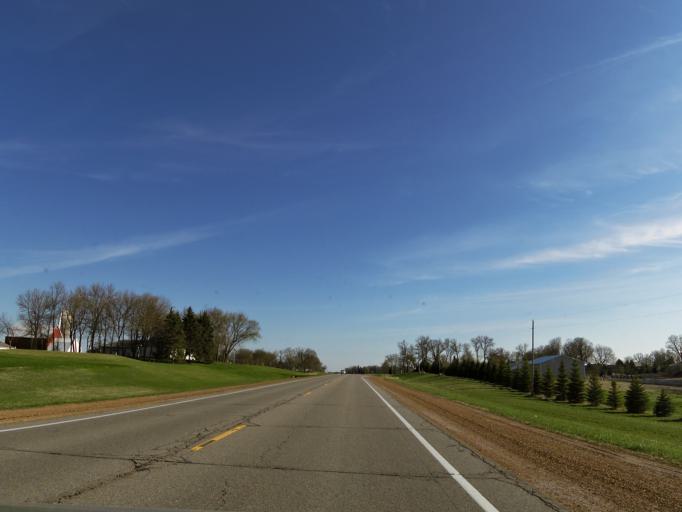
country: US
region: Minnesota
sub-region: Scott County
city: Prior Lake
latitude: 44.6402
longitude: -93.5015
